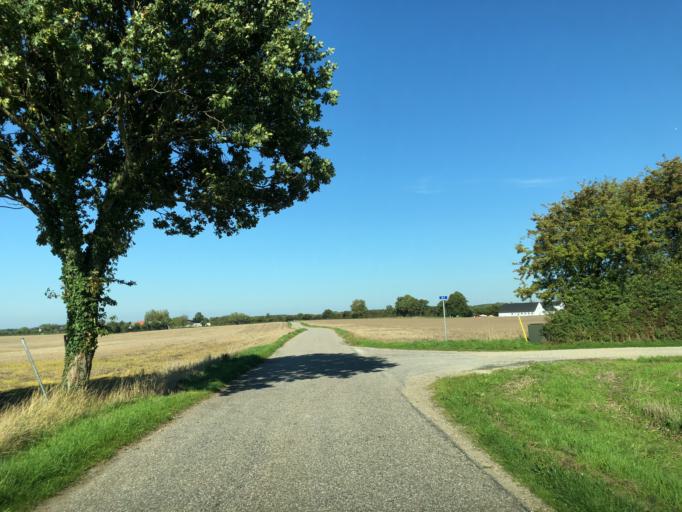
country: DK
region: South Denmark
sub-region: Sonderborg Kommune
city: Dybbol
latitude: 54.9417
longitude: 9.7318
